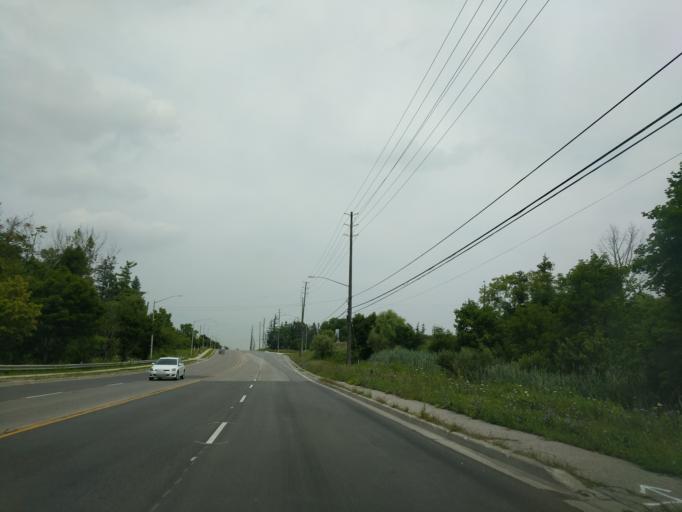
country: CA
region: Ontario
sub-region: York
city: Richmond Hill
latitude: 43.8838
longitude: -79.3920
